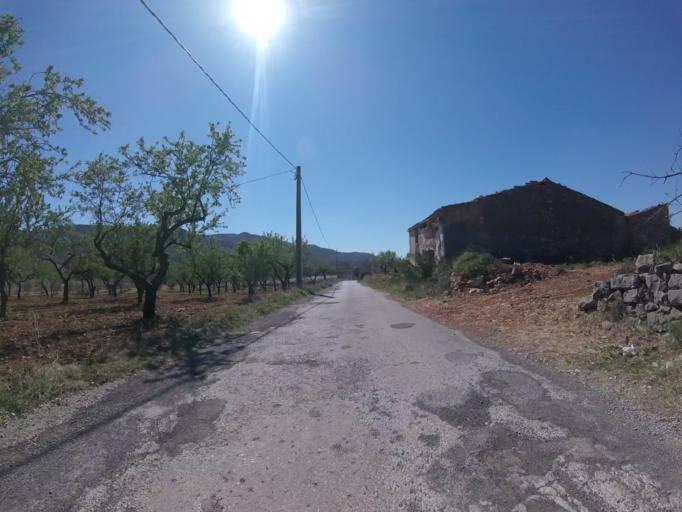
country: ES
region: Valencia
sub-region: Provincia de Castello
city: Chert/Xert
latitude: 40.4147
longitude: 0.1750
